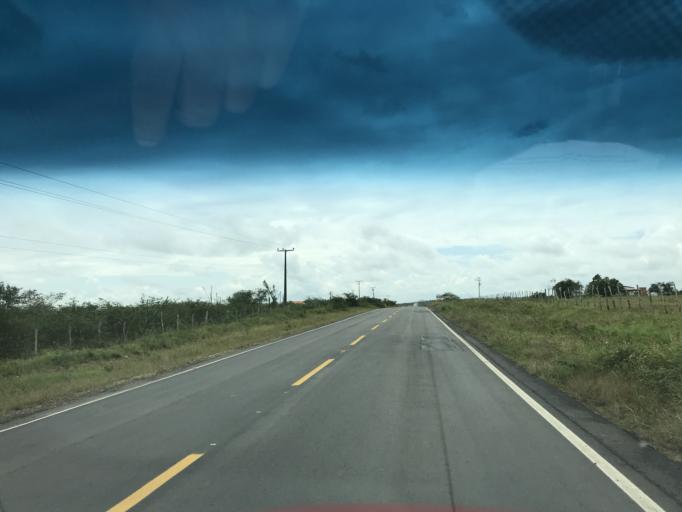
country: BR
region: Bahia
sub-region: Castro Alves
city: Castro Alves
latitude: -12.6823
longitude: -39.3056
